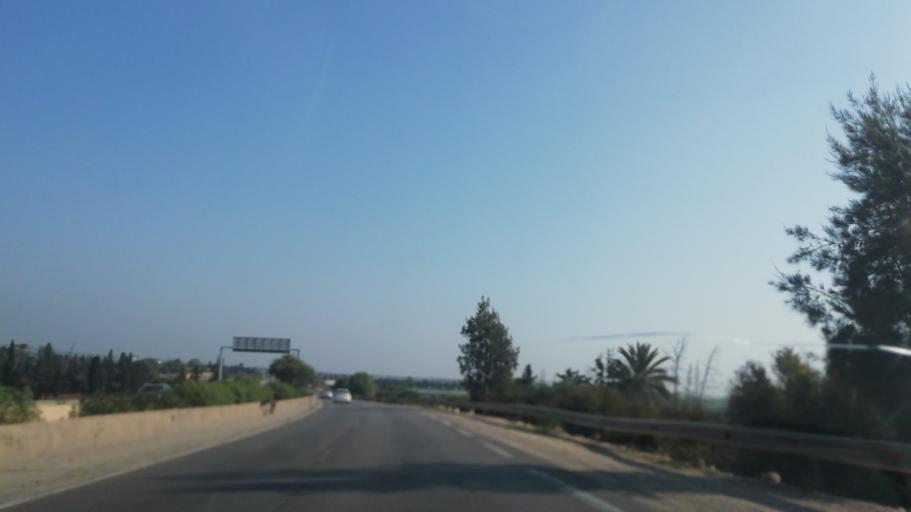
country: DZ
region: Oran
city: Bou Tlelis
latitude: 35.5659
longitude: -0.9033
